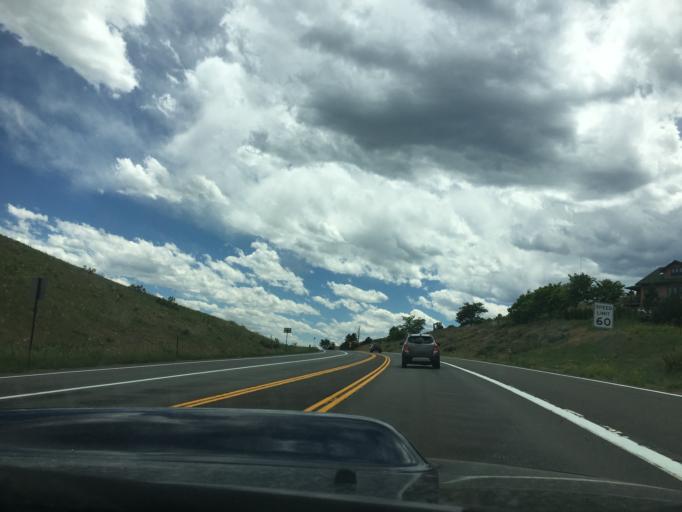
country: US
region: Colorado
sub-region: Boulder County
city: Lyons
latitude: 40.1877
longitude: -105.2523
